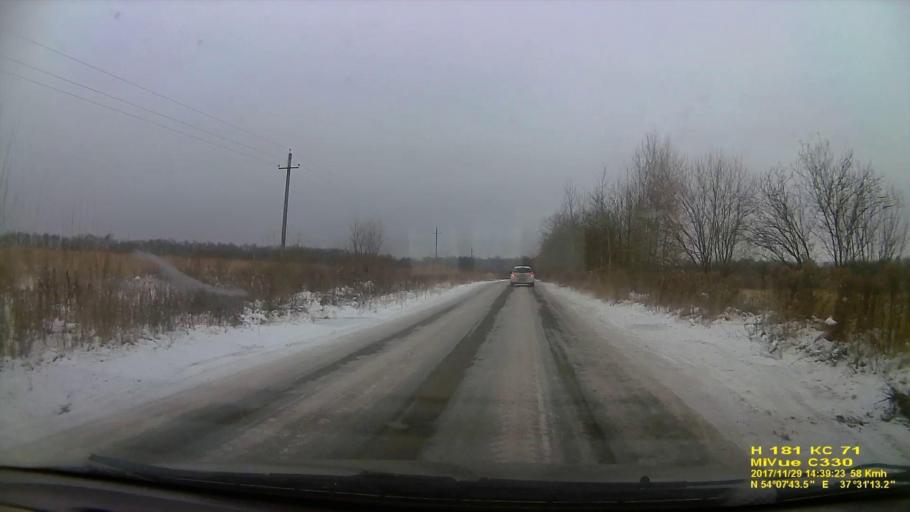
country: RU
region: Tula
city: Kosaya Gora
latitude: 54.1287
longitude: 37.5203
